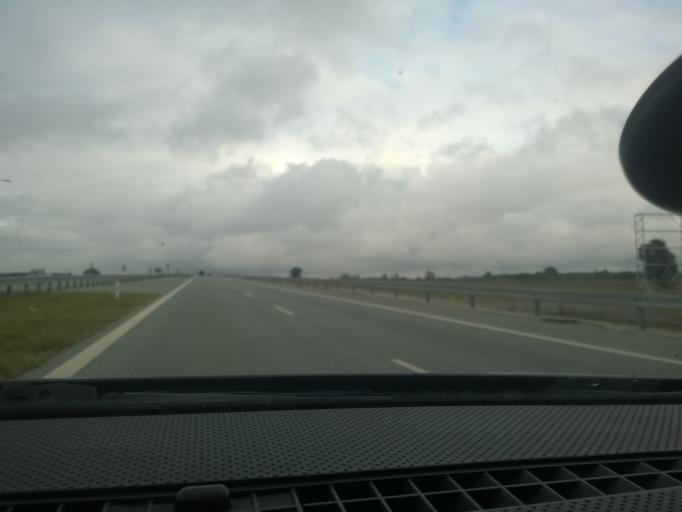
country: PL
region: Lodz Voivodeship
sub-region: Powiat zdunskowolski
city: Zapolice
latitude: 51.5942
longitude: 18.8323
